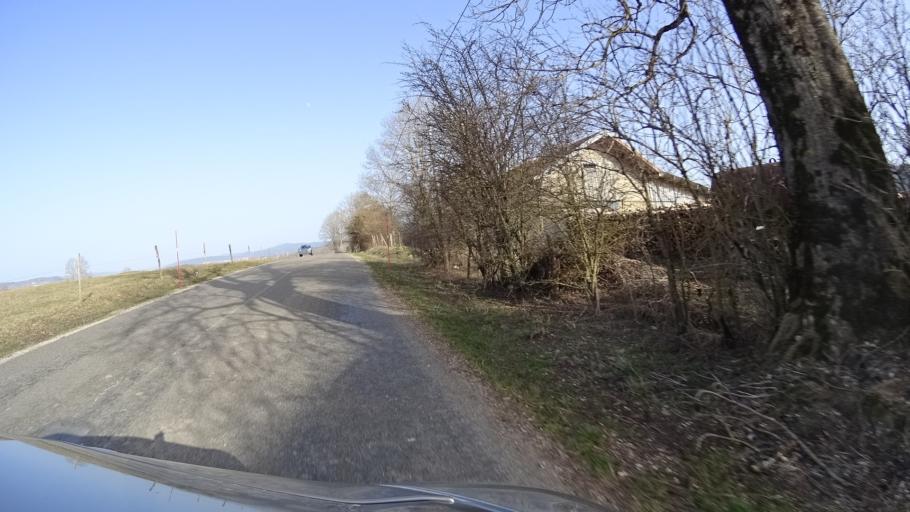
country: FR
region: Franche-Comte
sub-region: Departement du Doubs
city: Frasne
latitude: 46.8661
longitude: 6.2273
